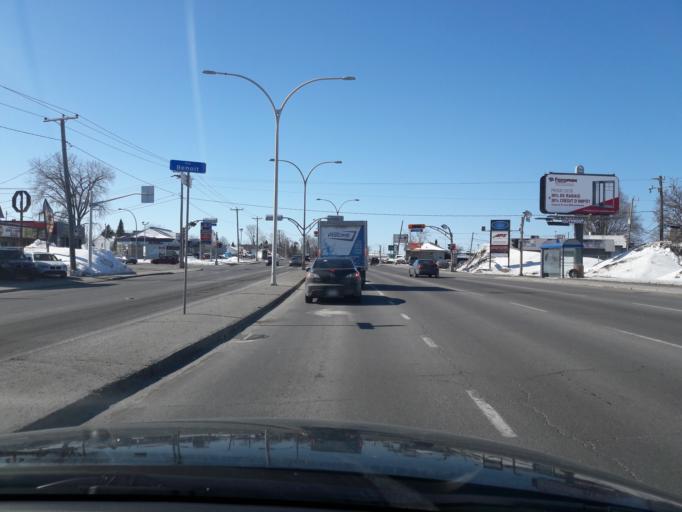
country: CA
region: Quebec
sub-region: Laurentides
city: Rosemere
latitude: 45.5608
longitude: -73.7713
